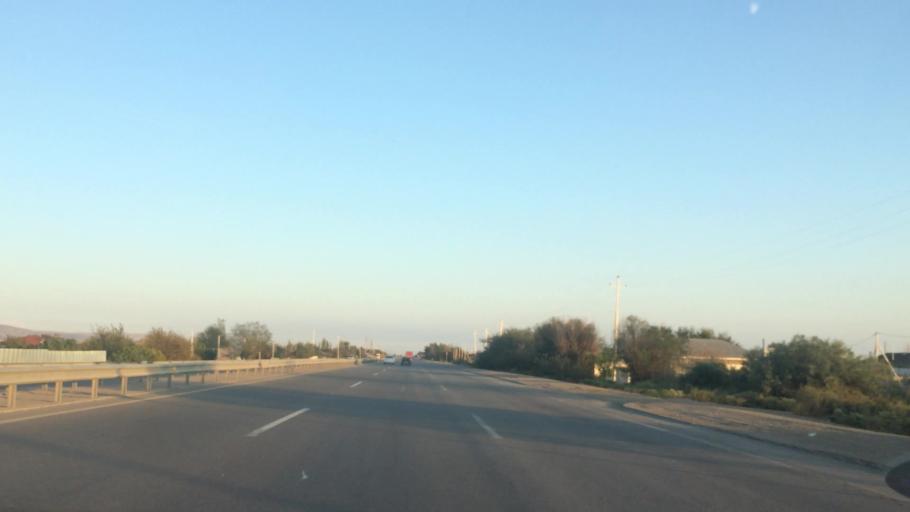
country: AZ
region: Haciqabul
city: Haciqabul
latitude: 40.0186
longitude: 49.1324
